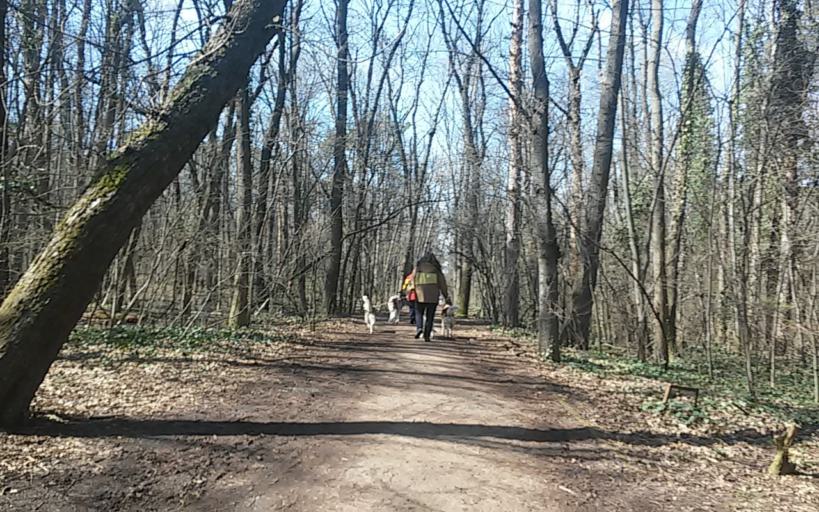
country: BG
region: Sofia-Capital
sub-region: Stolichna Obshtina
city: Sofia
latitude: 42.6796
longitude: 23.3495
